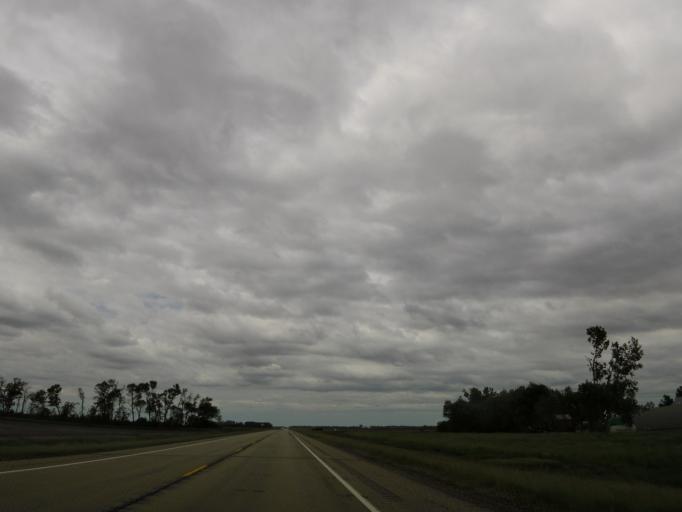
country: US
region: North Dakota
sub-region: Walsh County
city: Grafton
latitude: 48.5407
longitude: -97.4480
